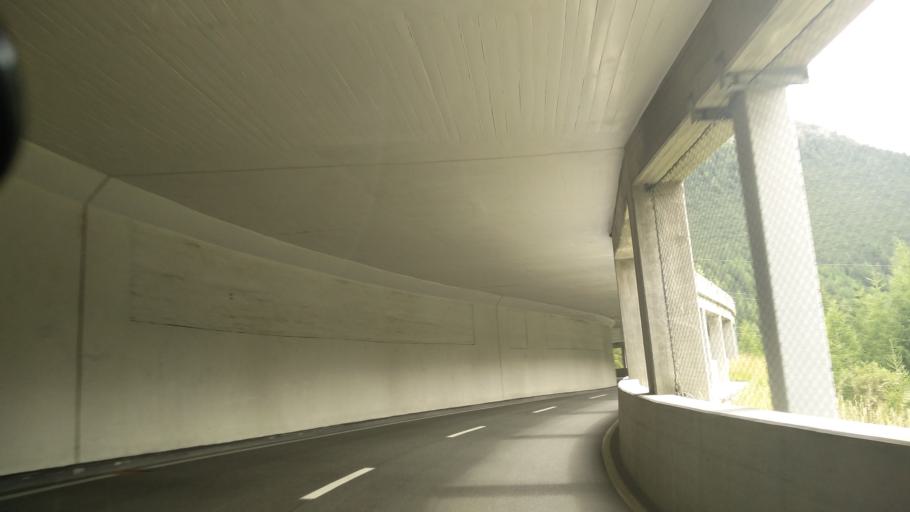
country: CH
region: Grisons
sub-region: Inn District
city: Zernez
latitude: 46.6948
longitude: 10.1225
